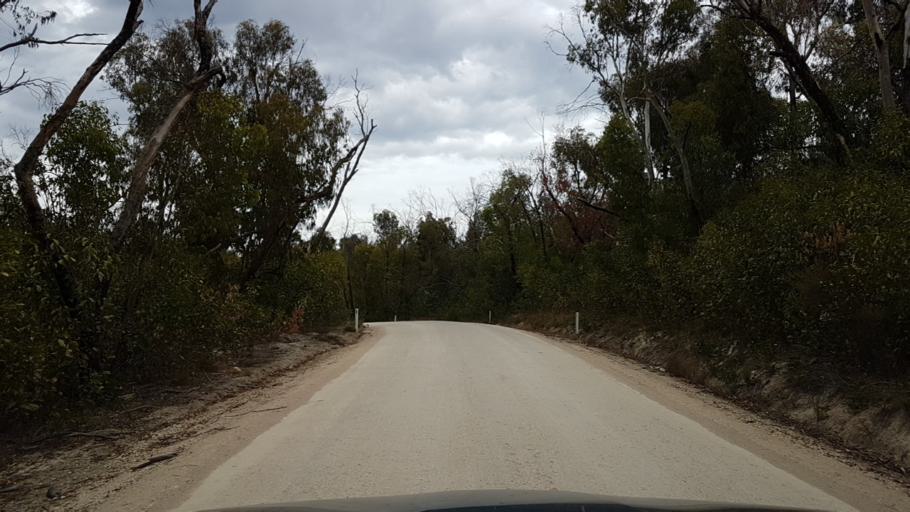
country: AU
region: South Australia
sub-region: Adelaide Hills
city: Gumeracha
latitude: -34.7897
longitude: 138.8359
